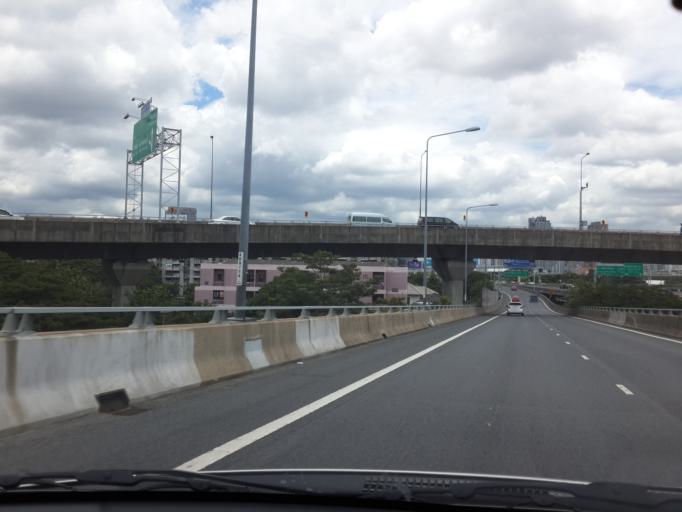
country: TH
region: Bangkok
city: Din Daeng
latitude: 13.7571
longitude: 100.5501
